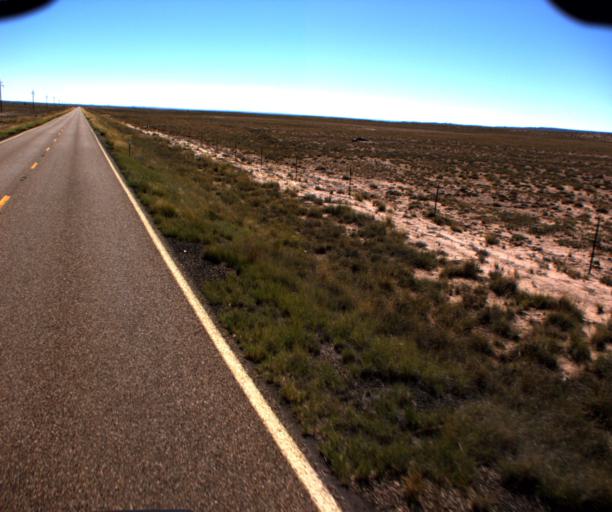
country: US
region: Arizona
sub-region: Navajo County
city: Holbrook
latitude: 35.1243
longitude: -110.0922
